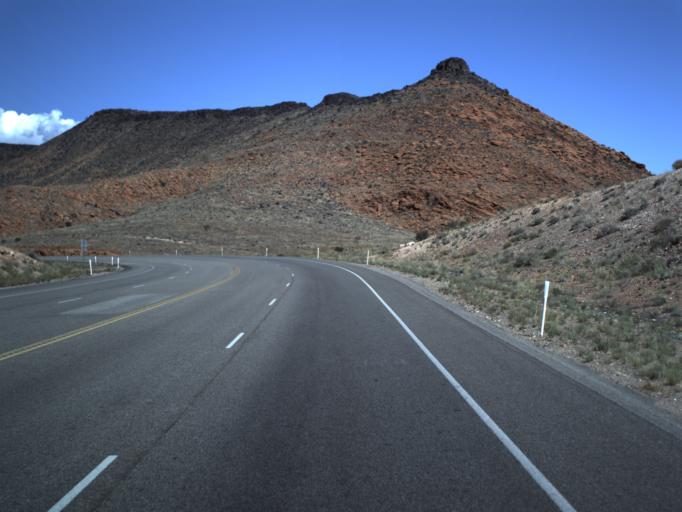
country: US
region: Utah
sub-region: Washington County
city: Saint George
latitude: 37.1555
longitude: -113.6037
